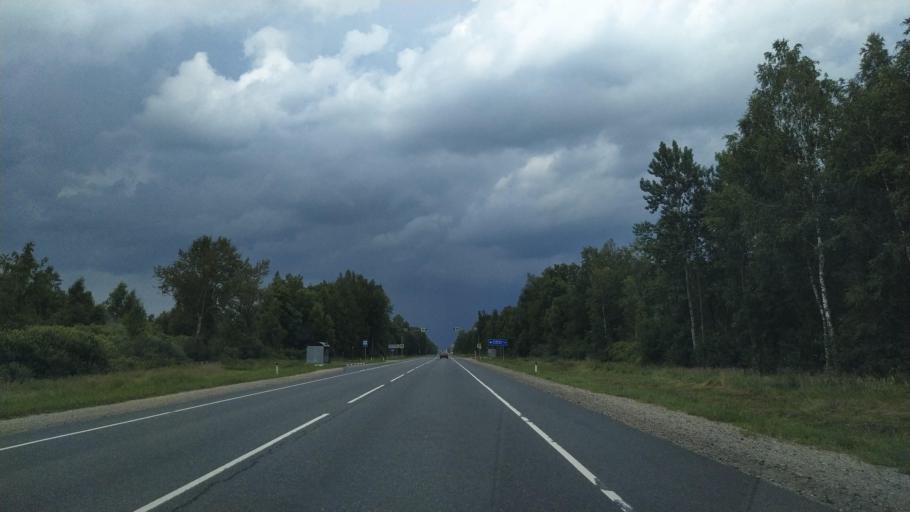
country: RU
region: Pskov
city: Pskov
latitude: 57.6078
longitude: 28.3211
